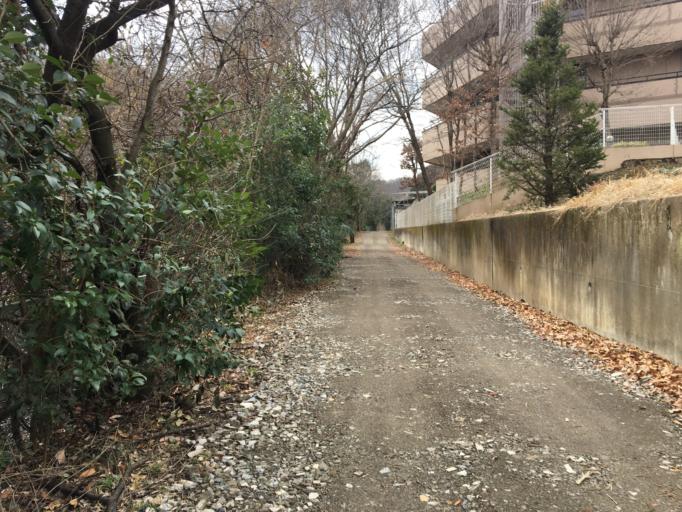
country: JP
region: Saitama
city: Oi
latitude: 35.8059
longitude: 139.5273
